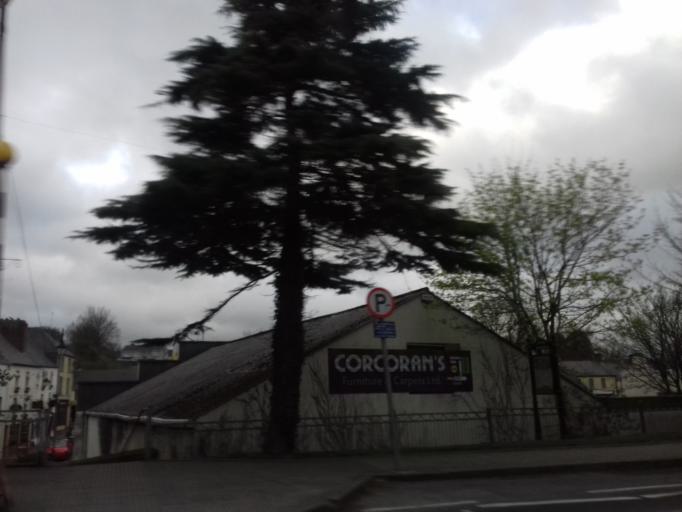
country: IE
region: Munster
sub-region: County Limerick
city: Newcastle West
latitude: 52.4493
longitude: -9.0585
